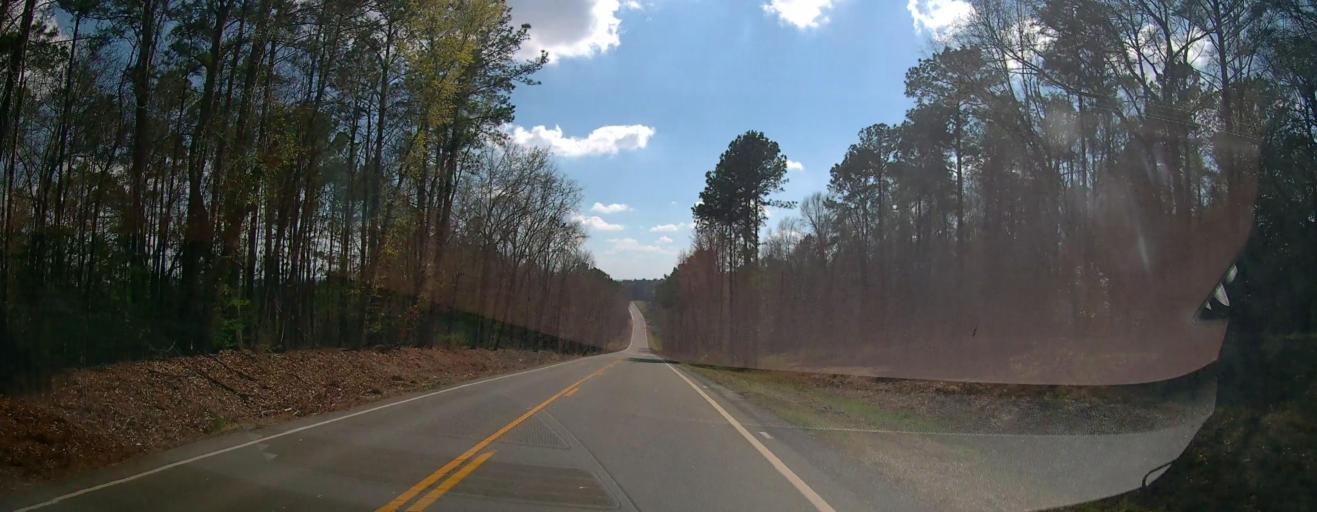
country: US
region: Georgia
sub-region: Wilkinson County
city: Gordon
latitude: 32.8033
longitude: -83.3278
